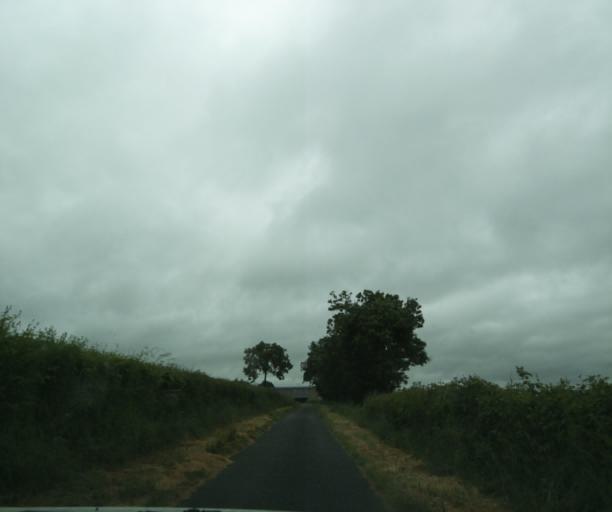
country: FR
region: Bourgogne
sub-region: Departement de Saone-et-Loire
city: Palinges
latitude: 46.5607
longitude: 4.2026
